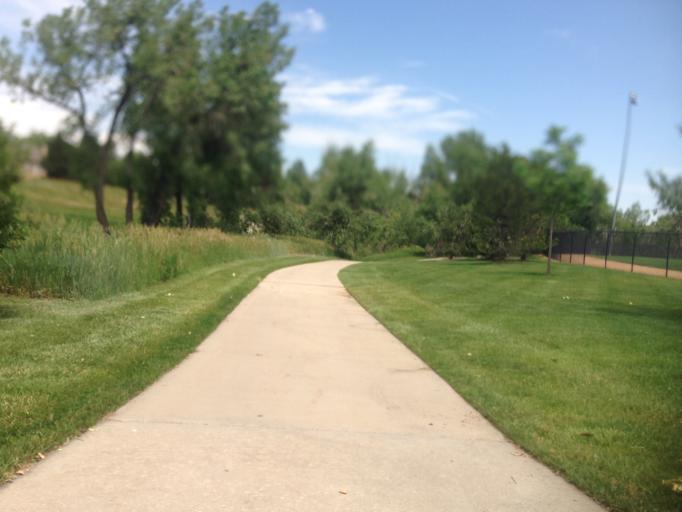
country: US
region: Colorado
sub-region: Boulder County
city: Superior
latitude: 39.9306
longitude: -105.1550
